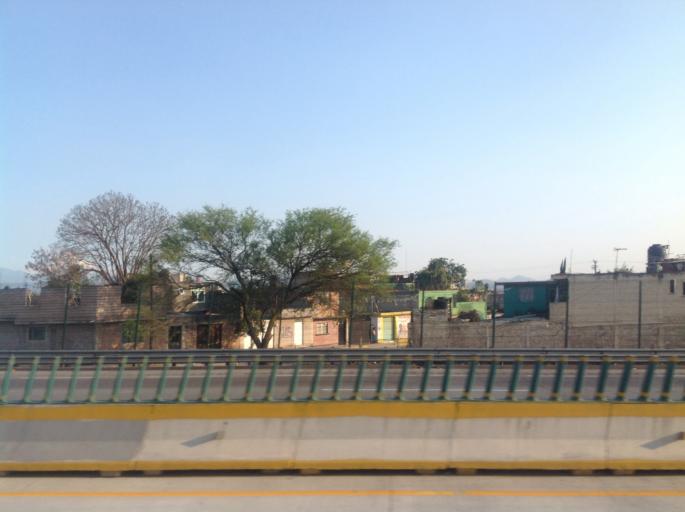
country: MX
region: Mexico
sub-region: Ixtapaluca
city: San Buenaventura
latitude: 19.2988
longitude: -98.8617
